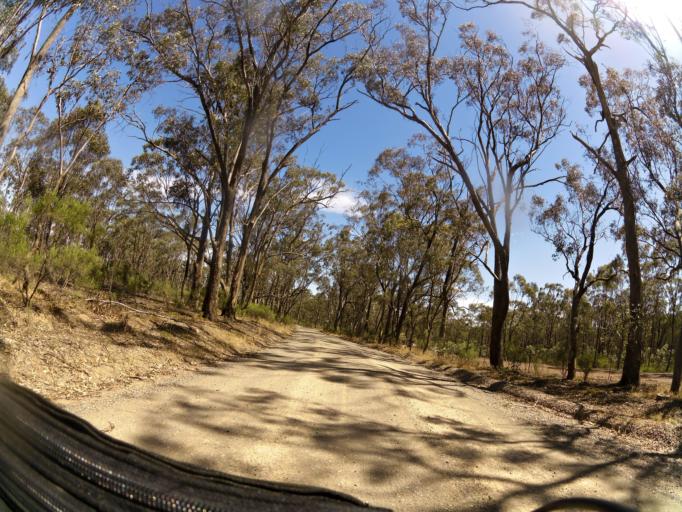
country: AU
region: Victoria
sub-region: Campaspe
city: Kyabram
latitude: -36.8437
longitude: 145.0667
